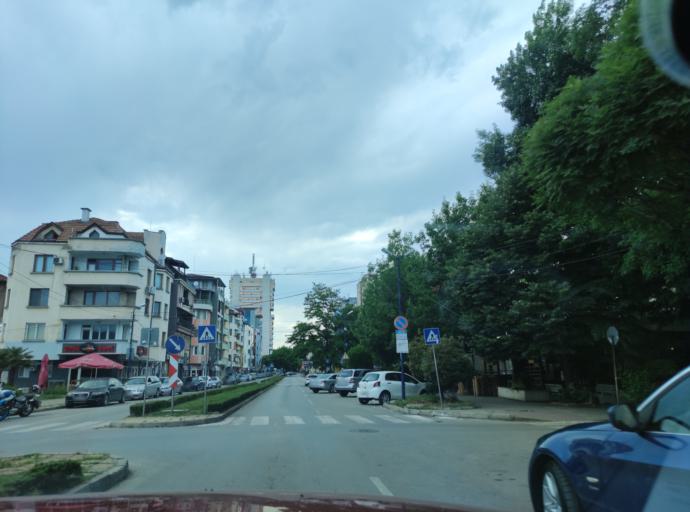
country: BG
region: Pazardzhik
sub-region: Obshtina Pazardzhik
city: Pazardzhik
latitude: 42.1867
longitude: 24.3344
